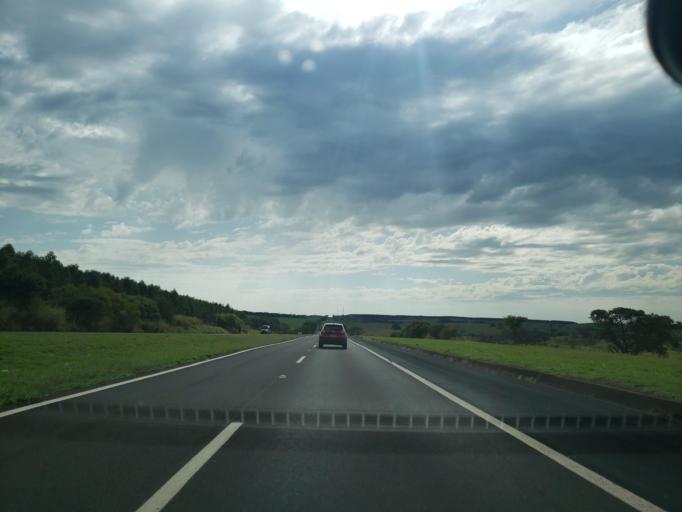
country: BR
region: Sao Paulo
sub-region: Cafelandia
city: Cafelandia
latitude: -21.7886
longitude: -49.6521
